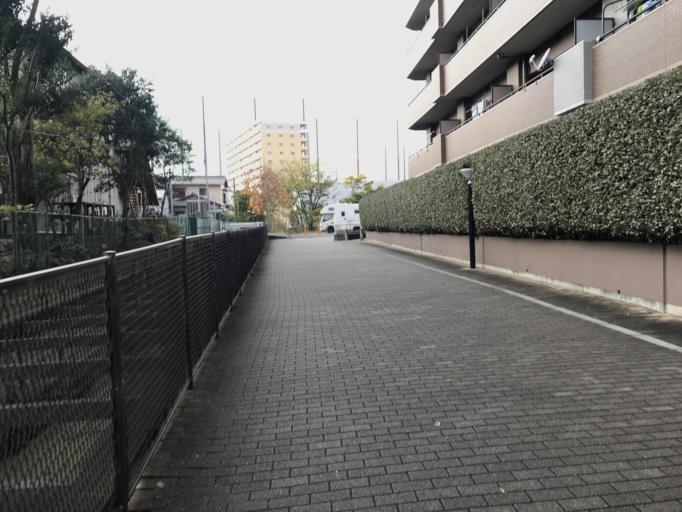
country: JP
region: Chiba
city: Funabashi
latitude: 35.7136
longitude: 139.9830
